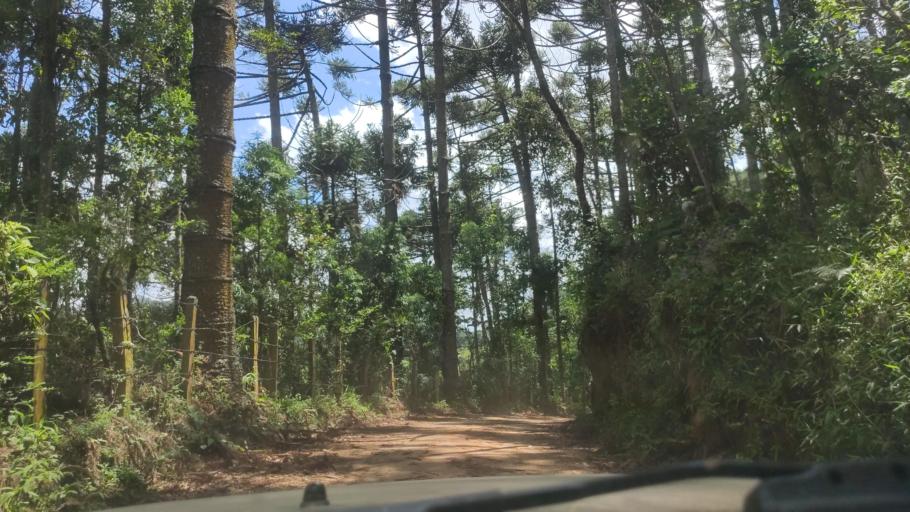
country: BR
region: Minas Gerais
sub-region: Cambui
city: Cambui
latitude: -22.6808
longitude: -45.9732
